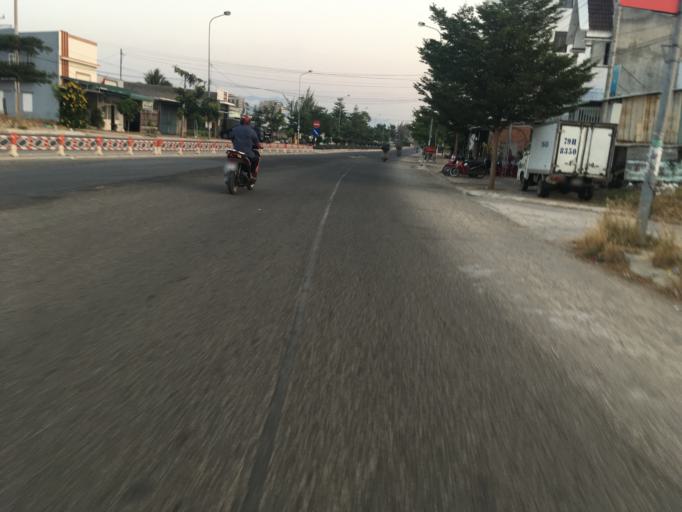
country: VN
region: Ninh Thuan
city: Phan Rang-Thap Cham
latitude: 11.5597
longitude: 109.0213
